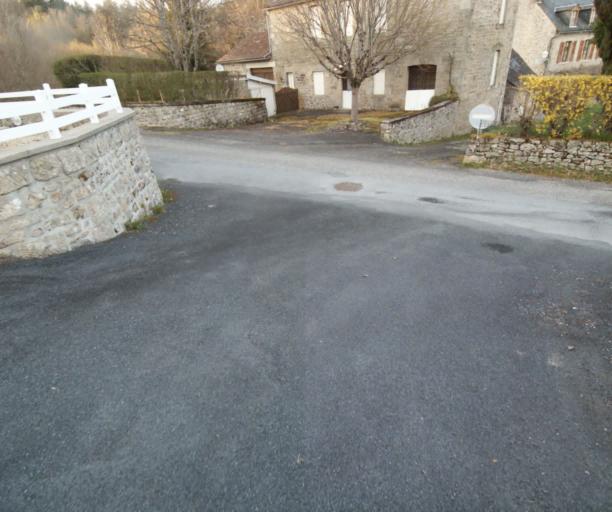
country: FR
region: Limousin
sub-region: Departement de la Correze
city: Argentat
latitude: 45.2461
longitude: 1.9824
